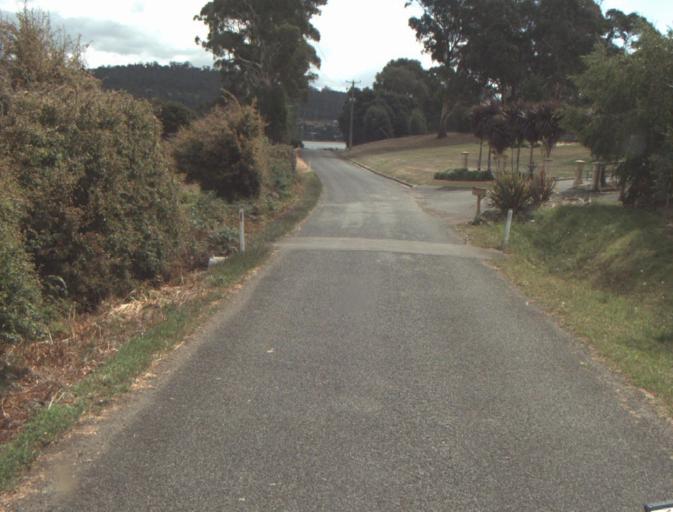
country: AU
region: Tasmania
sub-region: Launceston
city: Mayfield
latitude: -41.3159
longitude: 147.0019
